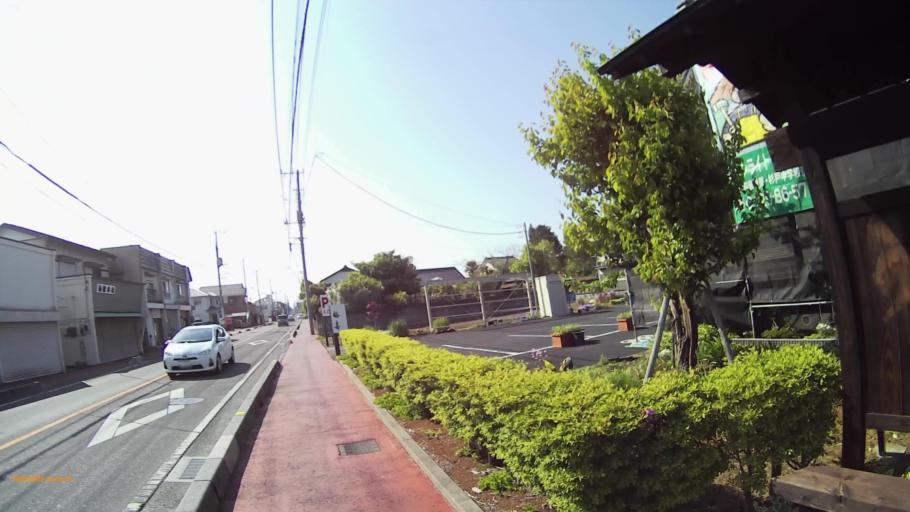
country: JP
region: Saitama
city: Sugito
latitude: 36.0261
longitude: 139.7347
